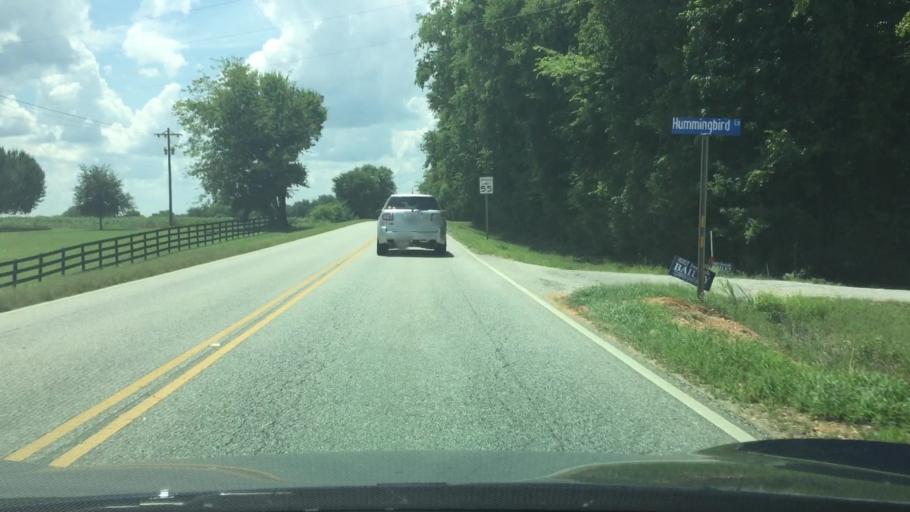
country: US
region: Alabama
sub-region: Montgomery County
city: Pike Road
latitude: 32.2484
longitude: -86.0933
